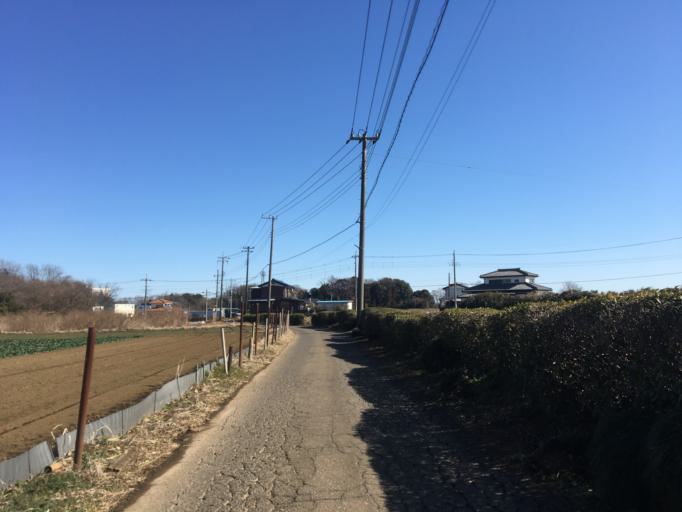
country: JP
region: Saitama
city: Oi
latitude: 35.8138
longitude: 139.5384
